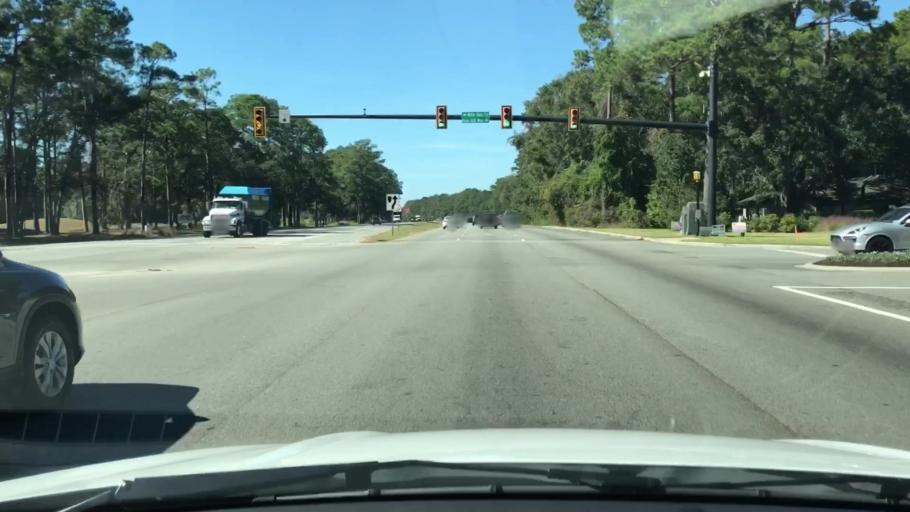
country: US
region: South Carolina
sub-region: Beaufort County
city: Bluffton
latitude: 32.2839
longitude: -80.8820
